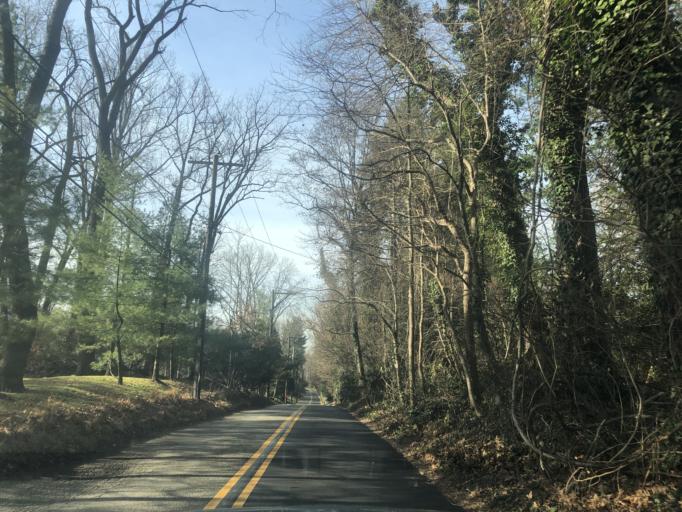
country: US
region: Pennsylvania
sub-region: Delaware County
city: Radnor
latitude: 40.0272
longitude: -75.3541
